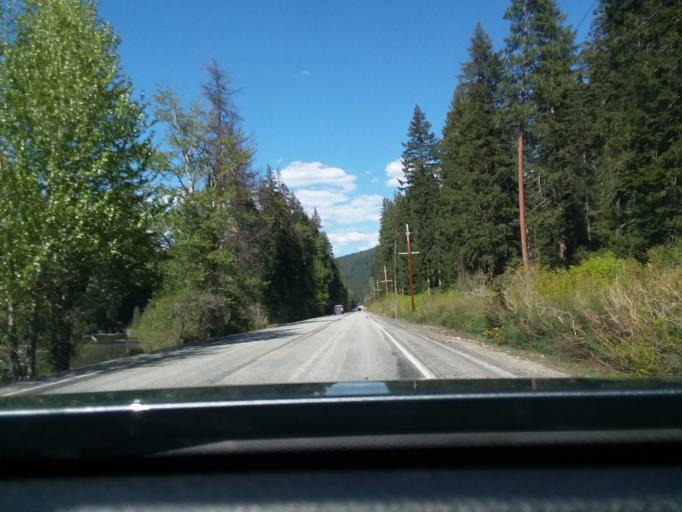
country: US
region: Washington
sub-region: Chelan County
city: Leavenworth
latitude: 47.7668
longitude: -120.7262
